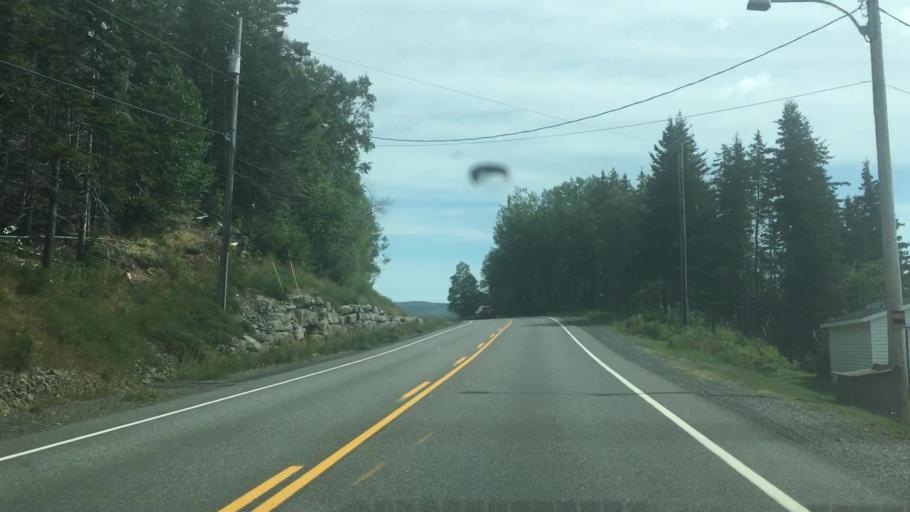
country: CA
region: Nova Scotia
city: Sydney Mines
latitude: 46.2656
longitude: -60.6142
